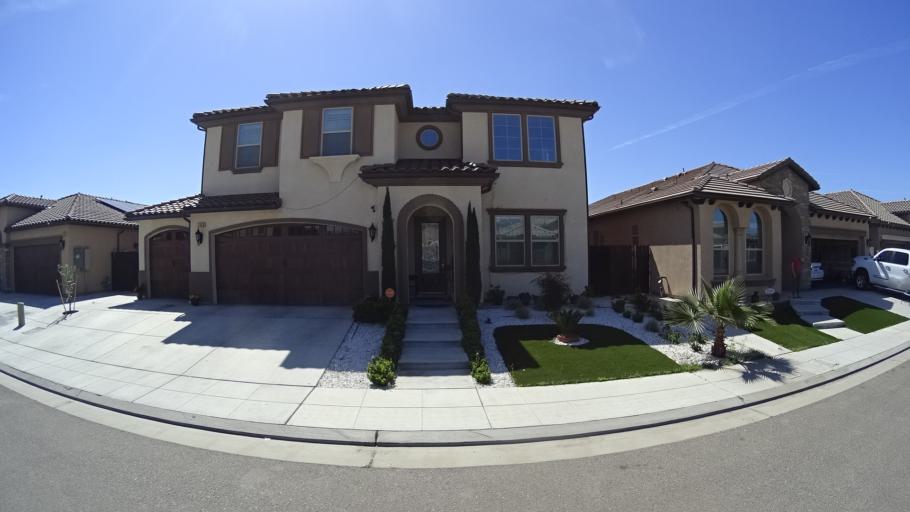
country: US
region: California
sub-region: Fresno County
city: Biola
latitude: 36.8194
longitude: -119.9224
